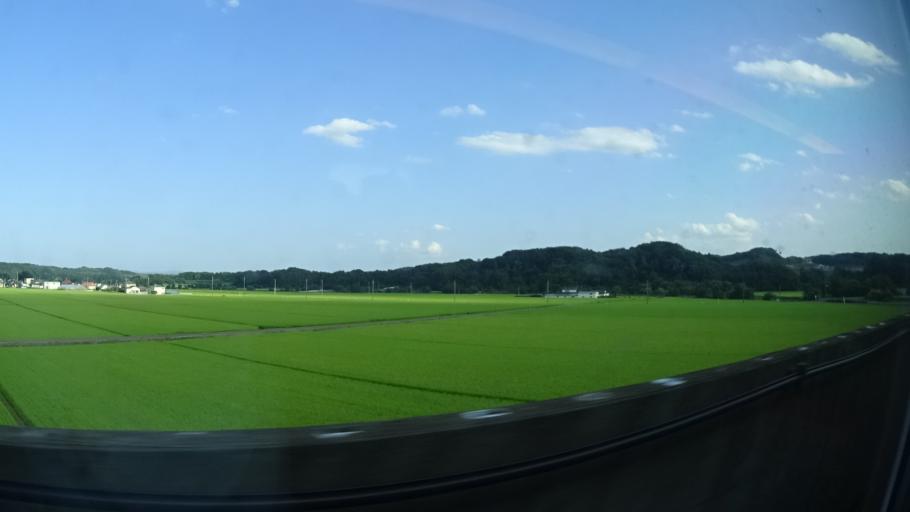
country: JP
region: Fukushima
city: Sukagawa
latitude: 37.2395
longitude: 140.2940
